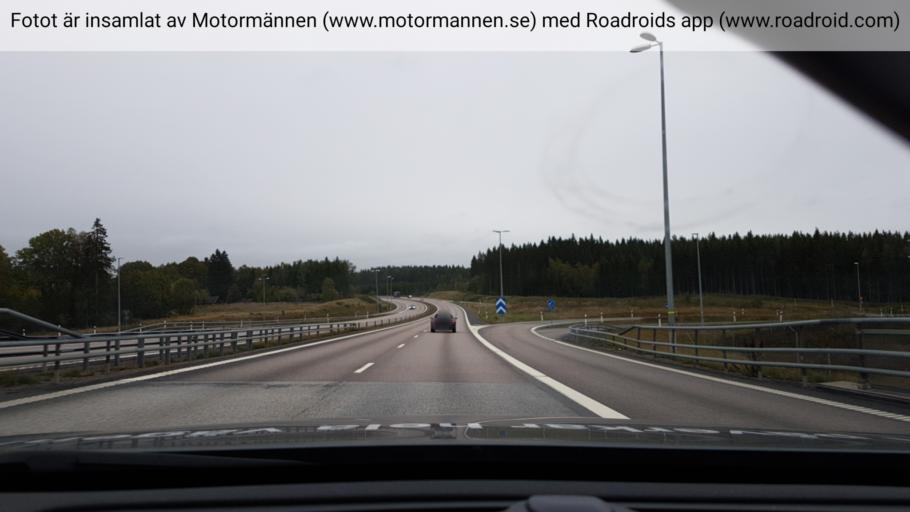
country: SE
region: Vaestra Goetaland
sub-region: Ulricehamns Kommun
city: Ulricehamn
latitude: 57.8186
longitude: 13.2858
